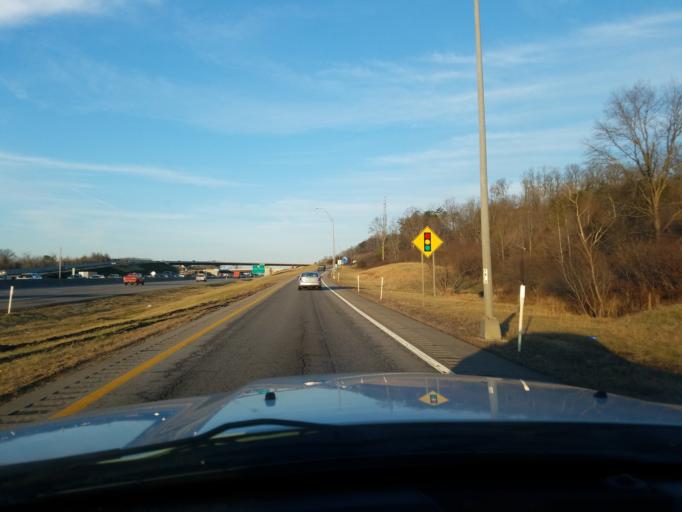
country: US
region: West Virginia
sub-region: Putnam County
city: Teays Valley
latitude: 38.4549
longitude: -81.8970
